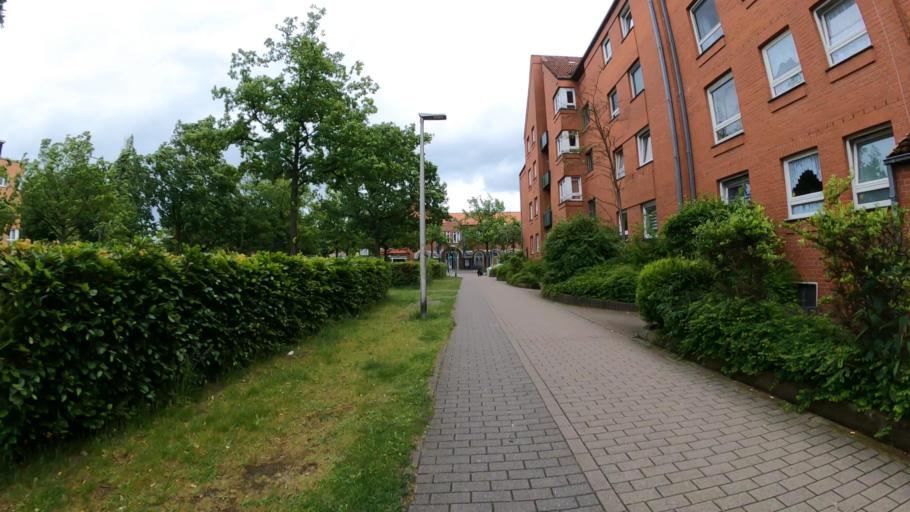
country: DE
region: Schleswig-Holstein
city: Norderstedt
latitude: 53.7075
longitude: 9.9874
